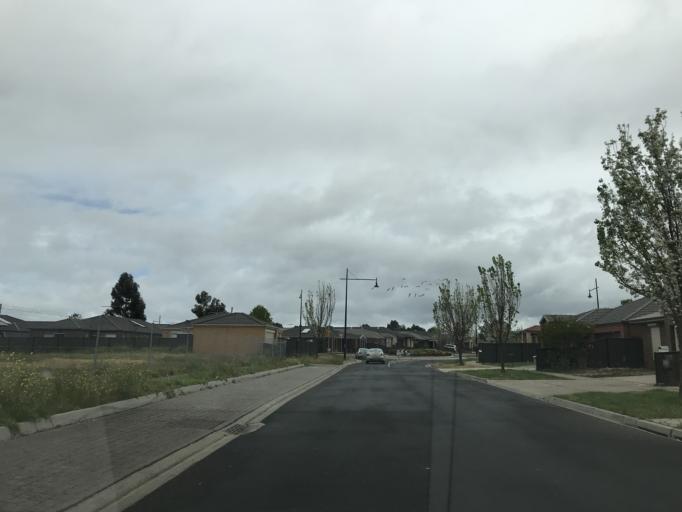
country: AU
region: Victoria
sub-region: Brimbank
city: Derrimut
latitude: -37.7896
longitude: 144.7594
